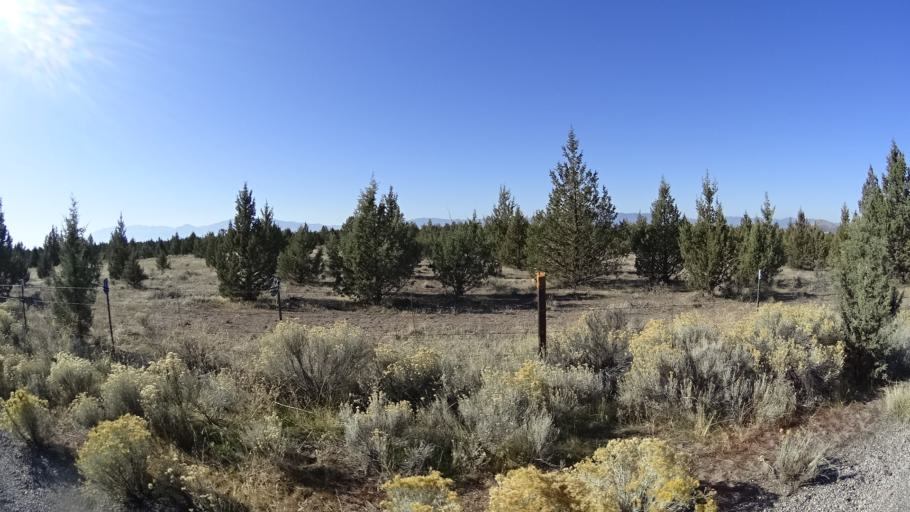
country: US
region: California
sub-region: Siskiyou County
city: Montague
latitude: 41.6387
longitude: -122.3411
